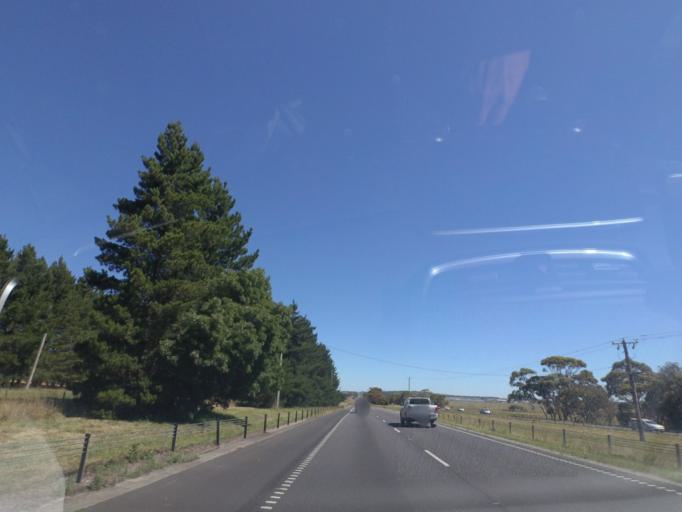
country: AU
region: Victoria
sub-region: Hume
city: Craigieburn
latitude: -37.5152
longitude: 144.9497
